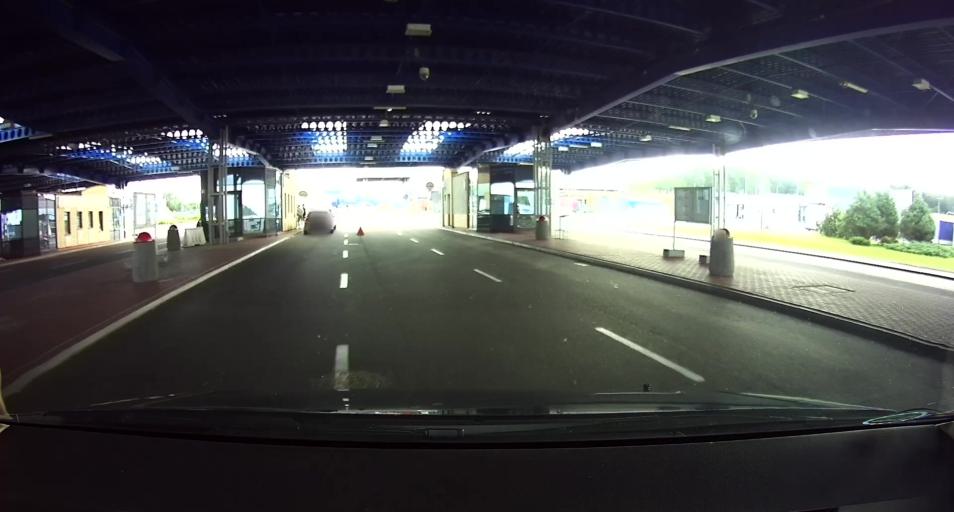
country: PL
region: Podlasie
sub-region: Powiat sokolski
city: Kuznica
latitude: 53.5205
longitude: 23.6574
